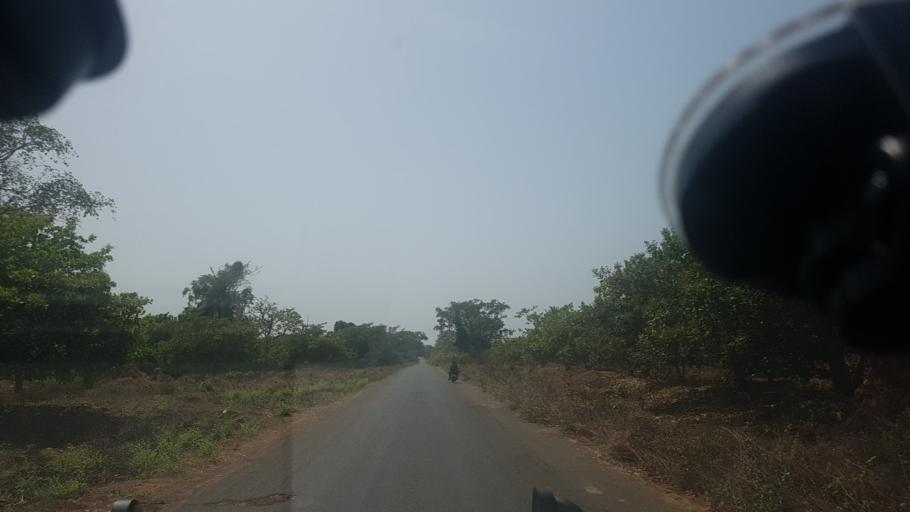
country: GW
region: Cacheu
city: Cacheu
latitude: 12.4097
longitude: -16.0370
